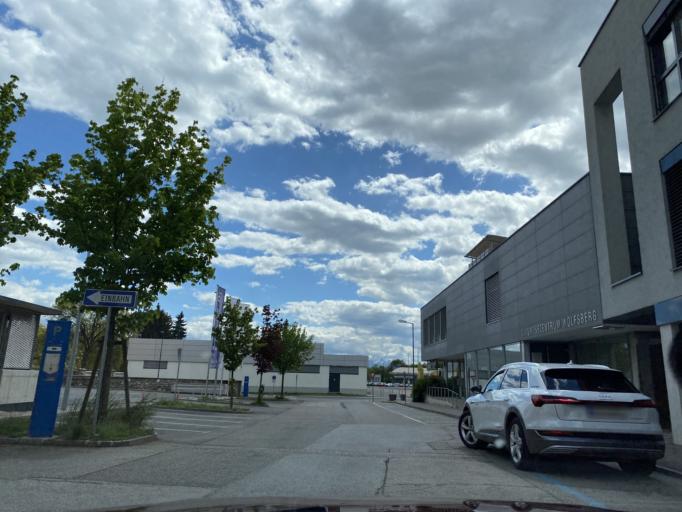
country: AT
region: Carinthia
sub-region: Politischer Bezirk Wolfsberg
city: Wolfsberg
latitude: 46.8390
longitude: 14.8409
